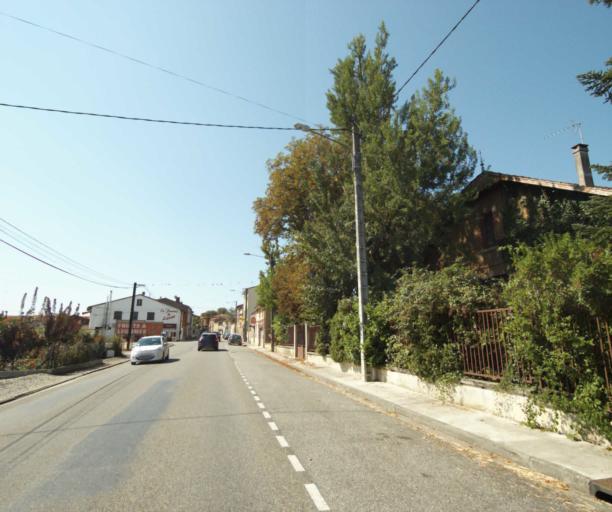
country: FR
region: Midi-Pyrenees
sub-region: Departement de l'Ariege
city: Lezat-sur-Leze
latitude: 43.2794
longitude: 1.3473
